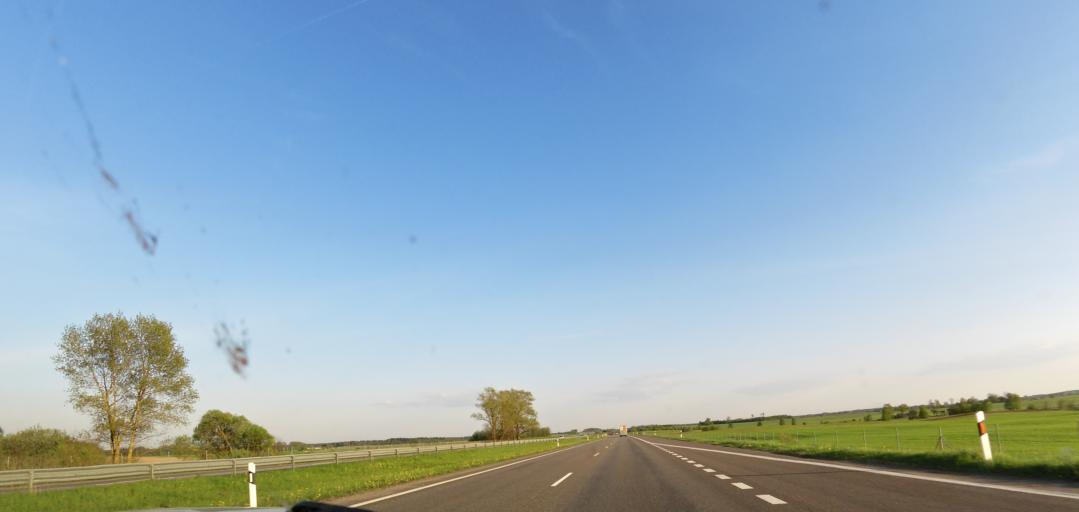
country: LT
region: Vilnius County
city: Ukmerge
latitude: 55.1564
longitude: 24.8209
